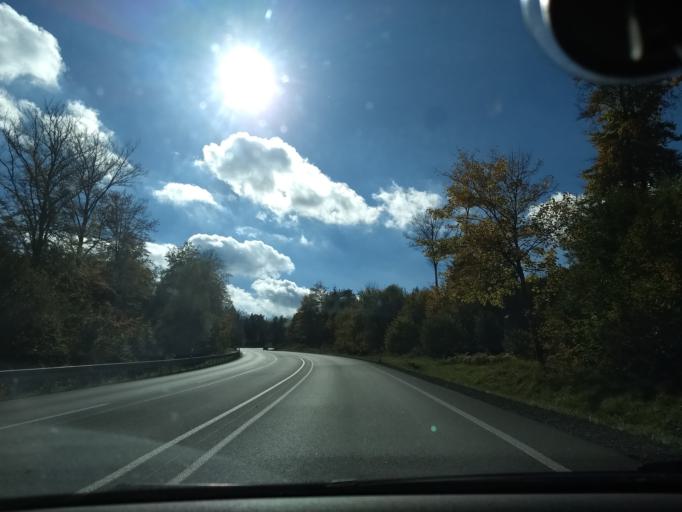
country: DE
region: North Rhine-Westphalia
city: Warstein
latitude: 51.4141
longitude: 8.3253
